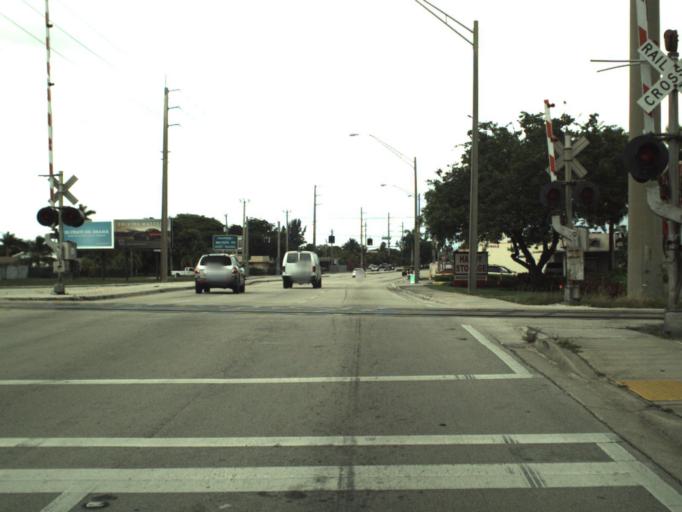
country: US
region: Florida
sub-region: Broward County
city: Dania Beach
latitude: 26.0488
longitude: -80.1470
